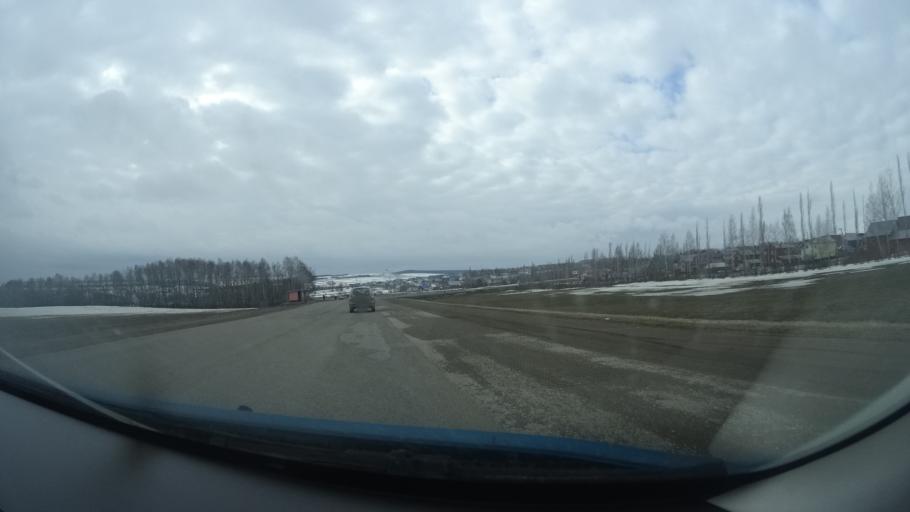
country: RU
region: Bashkortostan
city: Birsk
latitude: 55.4221
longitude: 55.5836
